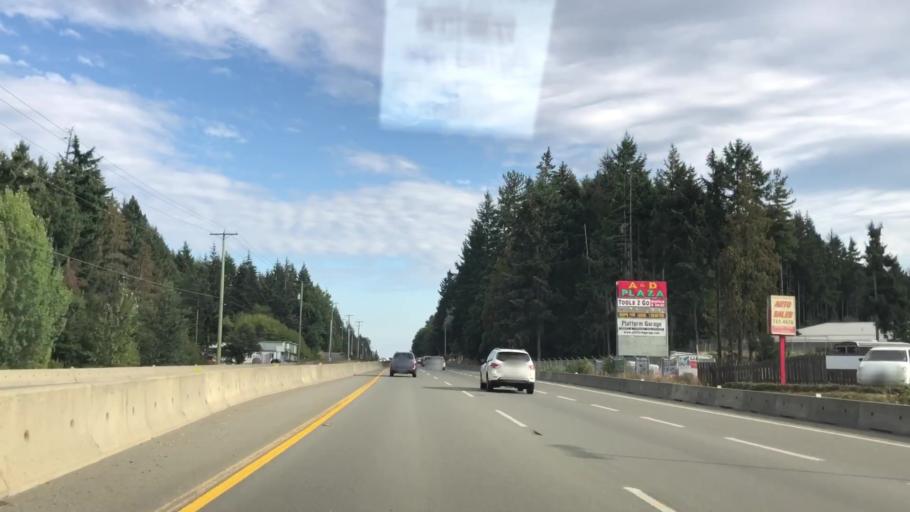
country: CA
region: British Columbia
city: Duncan
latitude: 48.6945
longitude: -123.5897
